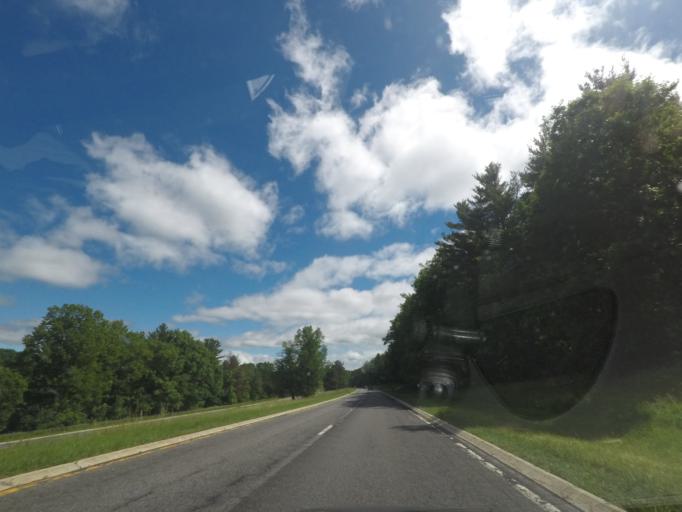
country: US
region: New York
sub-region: Columbia County
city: Chatham
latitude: 42.2998
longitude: -73.5826
